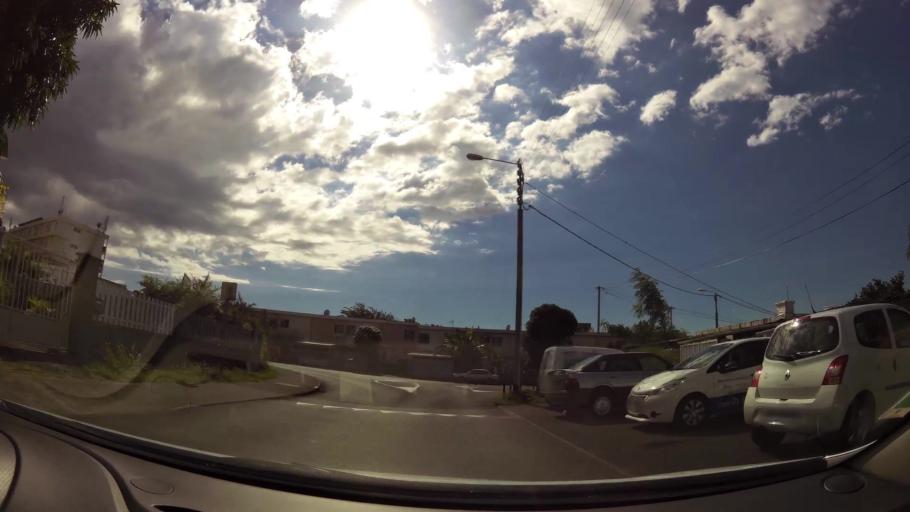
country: RE
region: Reunion
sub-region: Reunion
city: Saint-Denis
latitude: -20.8892
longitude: 55.4844
